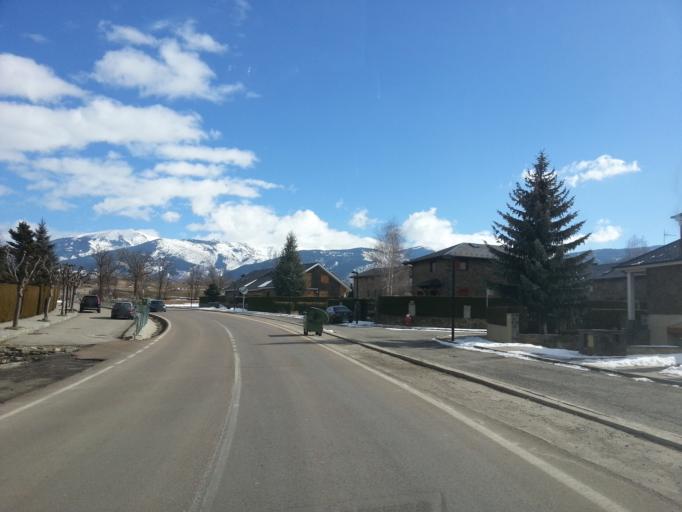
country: ES
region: Catalonia
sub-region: Provincia de Girona
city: Llivia
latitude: 42.4618
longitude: 1.9886
